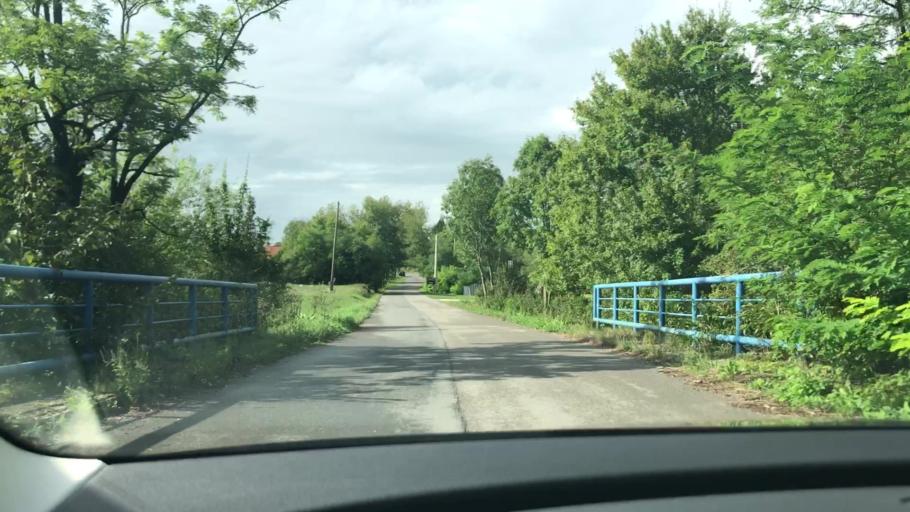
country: BA
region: Federation of Bosnia and Herzegovina
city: Izacic
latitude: 44.8754
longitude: 15.7167
